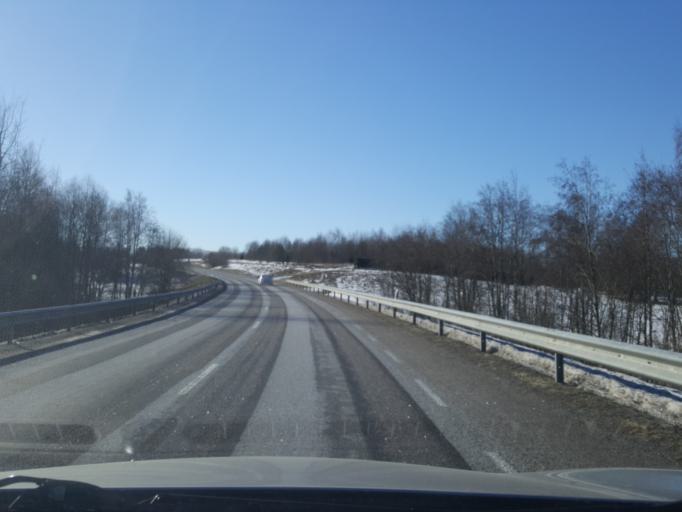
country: EE
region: Viljandimaa
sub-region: Viljandi linn
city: Viljandi
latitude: 58.3847
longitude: 25.6073
